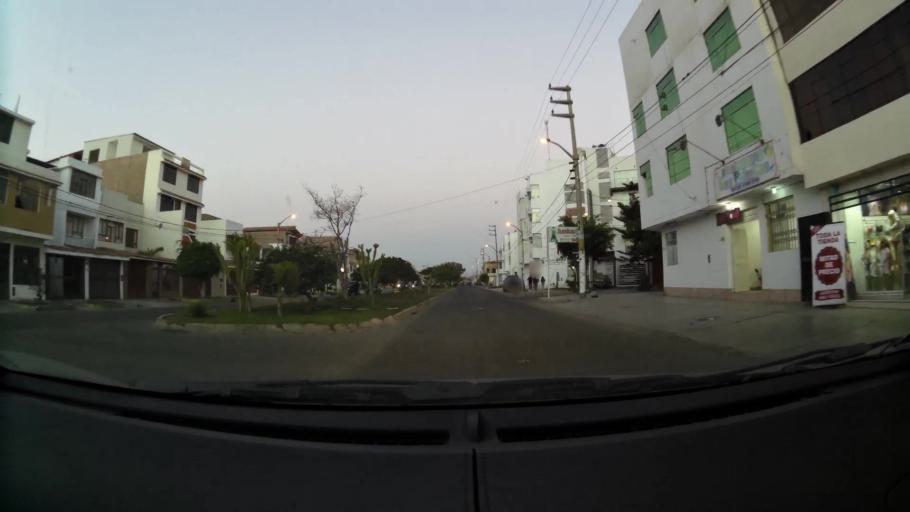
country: PE
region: Ancash
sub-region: Provincia de Santa
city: Buenos Aires
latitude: -9.1229
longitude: -78.5276
